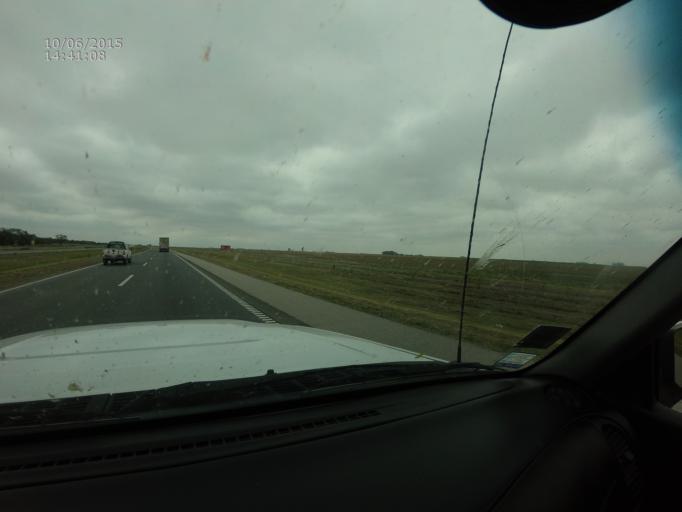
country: AR
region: Cordoba
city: Oliva
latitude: -32.0513
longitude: -63.5084
